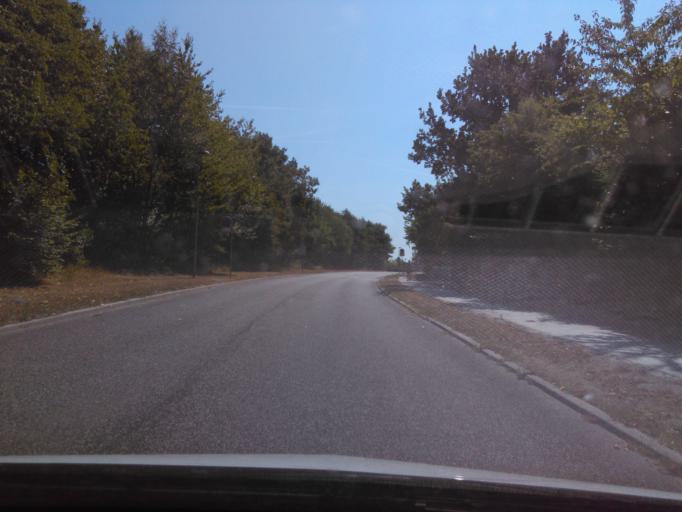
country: DK
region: Capital Region
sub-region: Fureso Kommune
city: Stavnsholt
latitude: 55.8222
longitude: 12.3869
